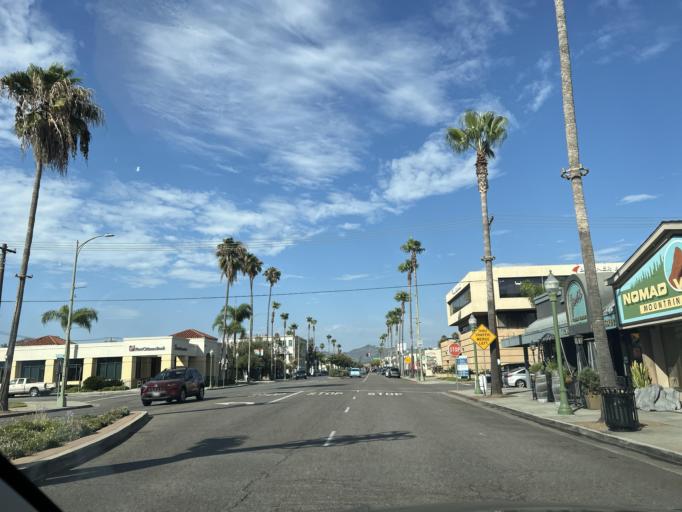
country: US
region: California
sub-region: San Diego County
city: Escondido
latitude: 33.1194
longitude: -117.0860
